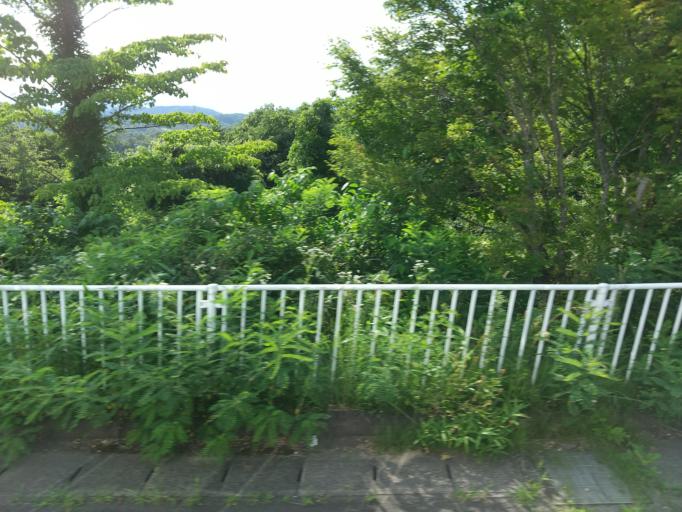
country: JP
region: Miyagi
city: Sendai
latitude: 38.2416
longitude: 140.7345
